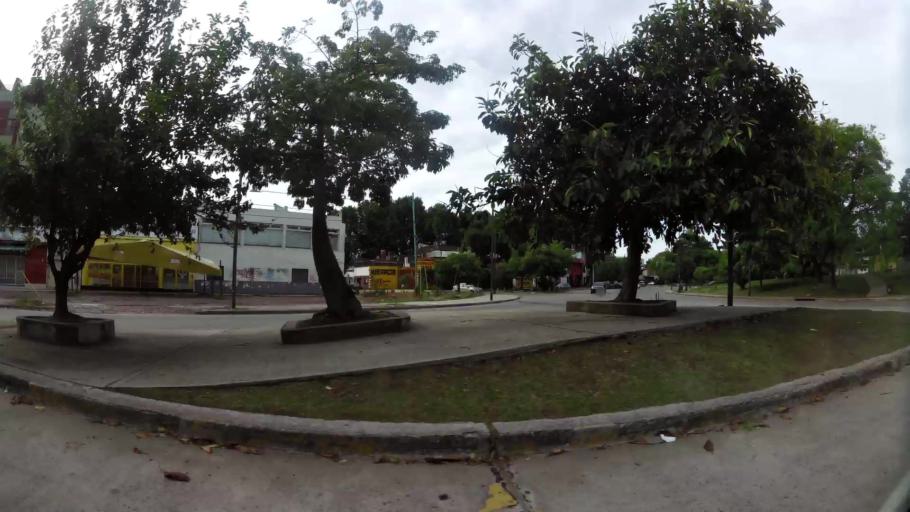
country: AR
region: Buenos Aires F.D.
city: Villa Lugano
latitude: -34.6439
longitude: -58.4628
